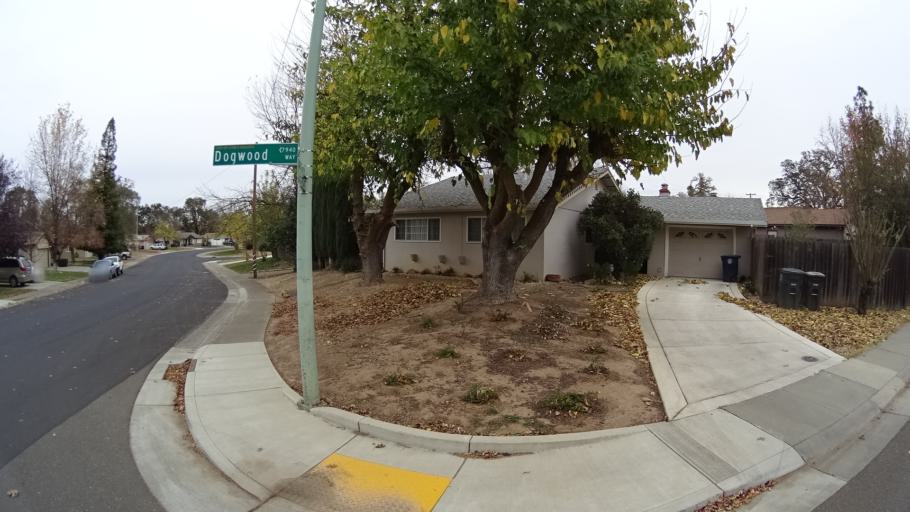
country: US
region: California
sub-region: Sacramento County
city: Citrus Heights
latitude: 38.7122
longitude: -121.2982
